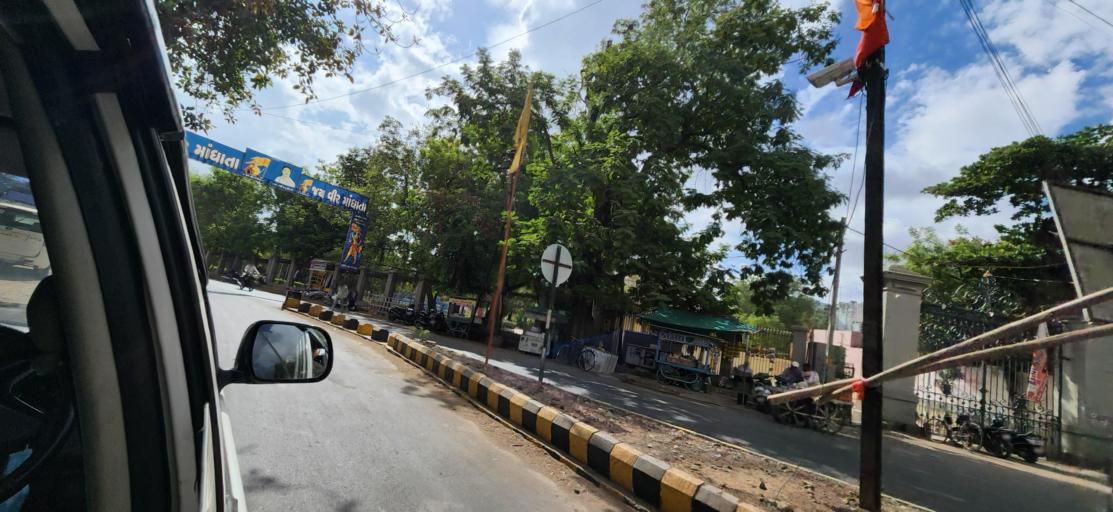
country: IN
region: Gujarat
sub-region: Bhavnagar
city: Bhavnagar
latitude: 21.7716
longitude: 72.1393
